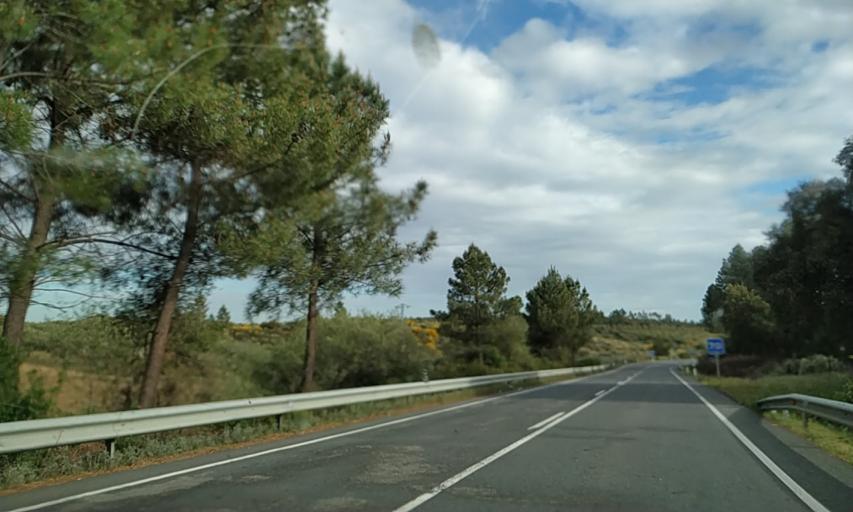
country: ES
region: Extremadura
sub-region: Provincia de Caceres
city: Perales del Puerto
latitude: 40.1488
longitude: -6.6769
